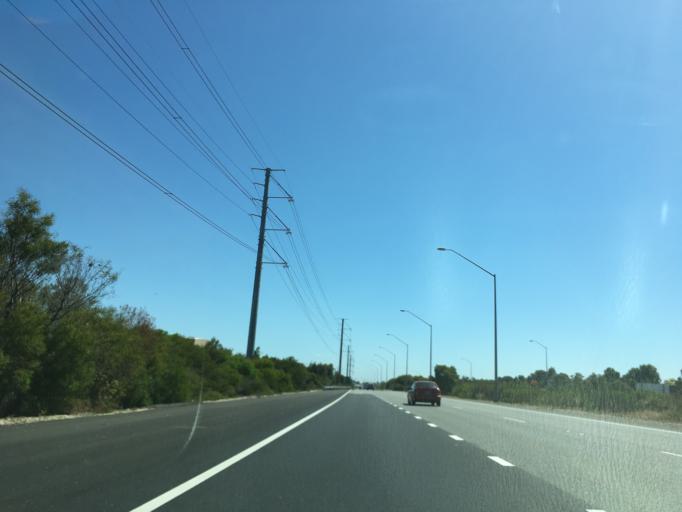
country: AU
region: Western Australia
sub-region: Canning
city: Willetton
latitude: -32.0597
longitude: 115.9019
